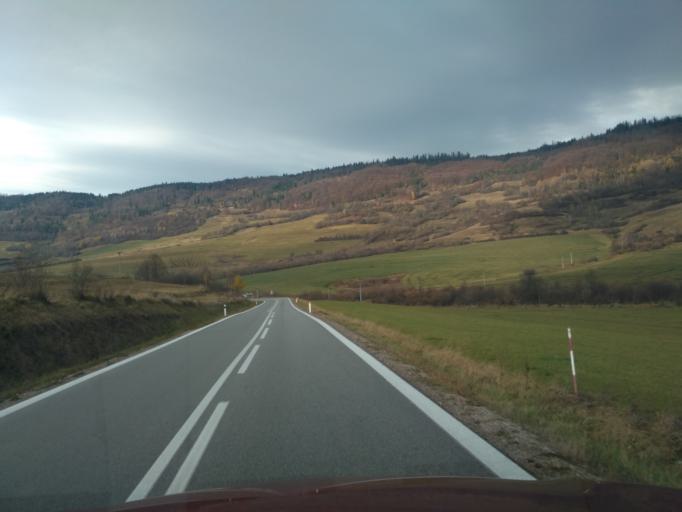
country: SK
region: Kosicky
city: Spisska Nova Ves
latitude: 48.8347
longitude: 20.6461
